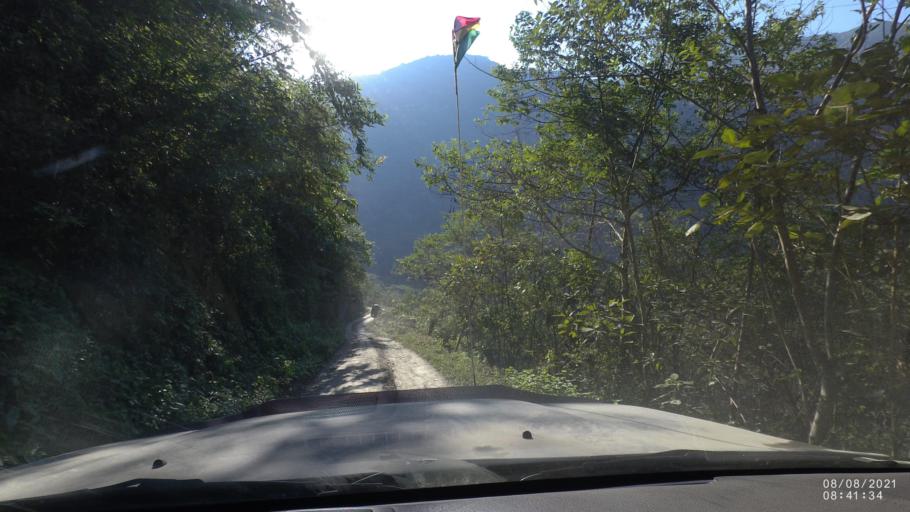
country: BO
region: La Paz
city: Quime
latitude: -16.5266
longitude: -66.7573
